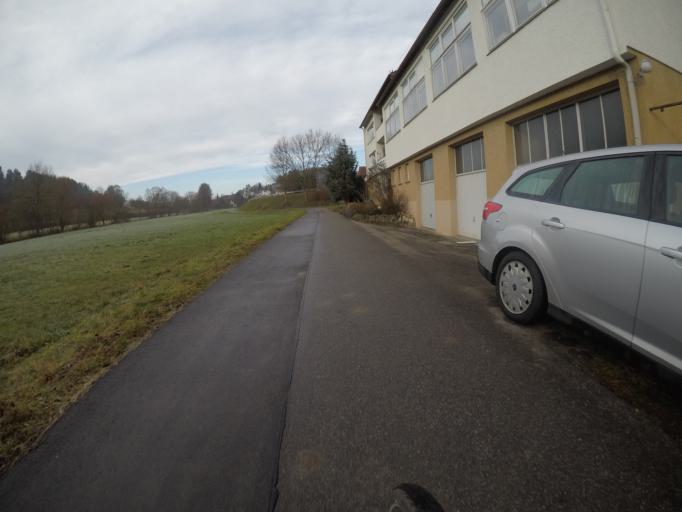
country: DE
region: Baden-Wuerttemberg
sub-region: Regierungsbezirk Stuttgart
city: Aidlingen
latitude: 48.6782
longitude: 8.8712
